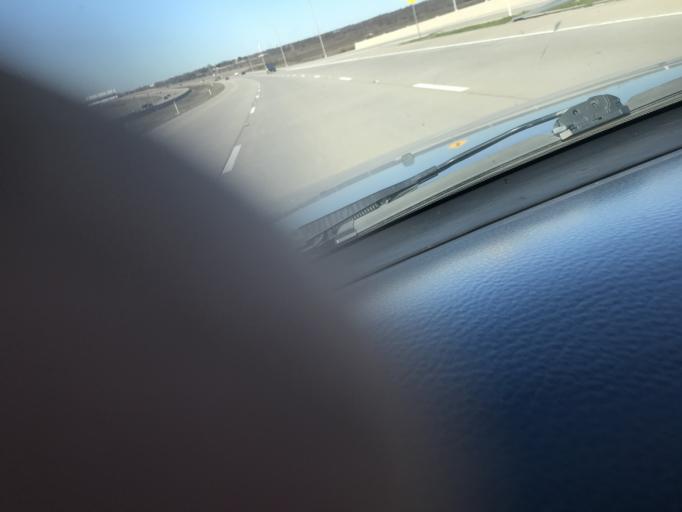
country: US
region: Texas
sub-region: Dallas County
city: Rowlett
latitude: 32.9343
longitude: -96.5526
